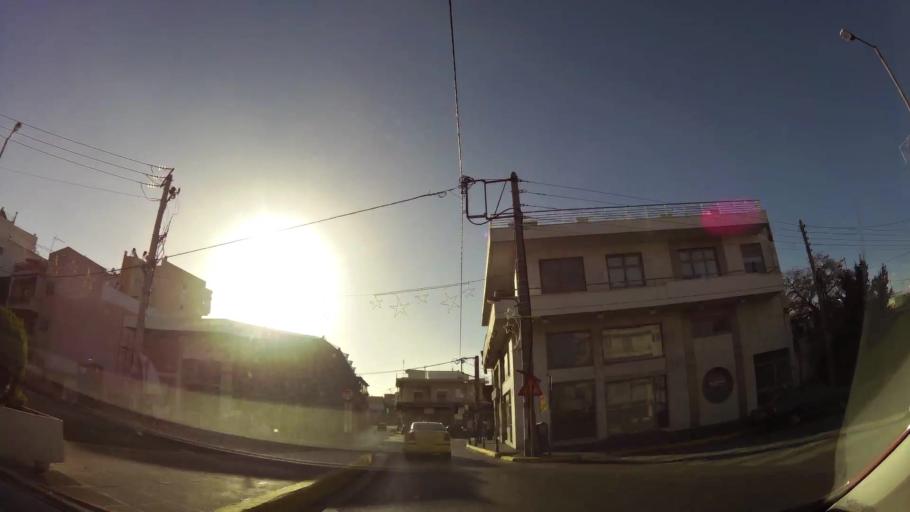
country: GR
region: Attica
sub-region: Nomarchia Anatolikis Attikis
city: Acharnes
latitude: 38.0789
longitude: 23.7377
